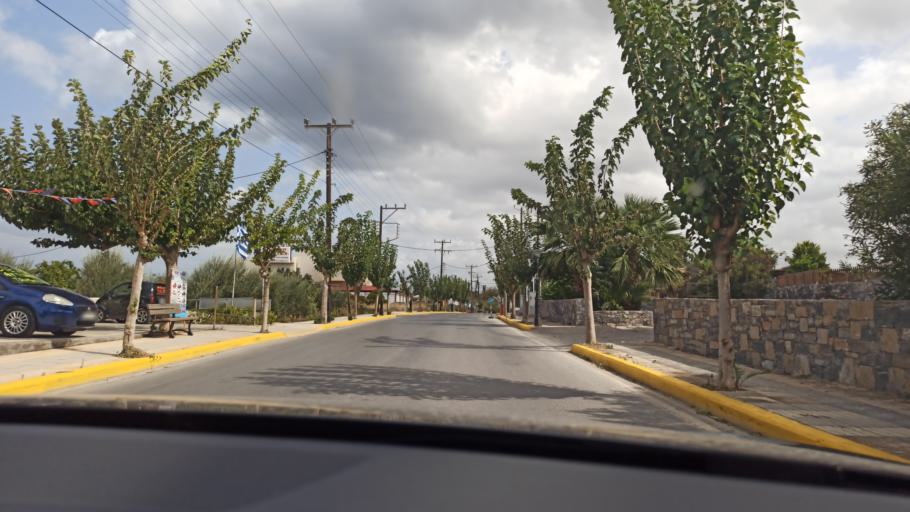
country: GR
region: Crete
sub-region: Nomos Irakleiou
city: Gazi
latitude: 35.3352
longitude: 25.0614
